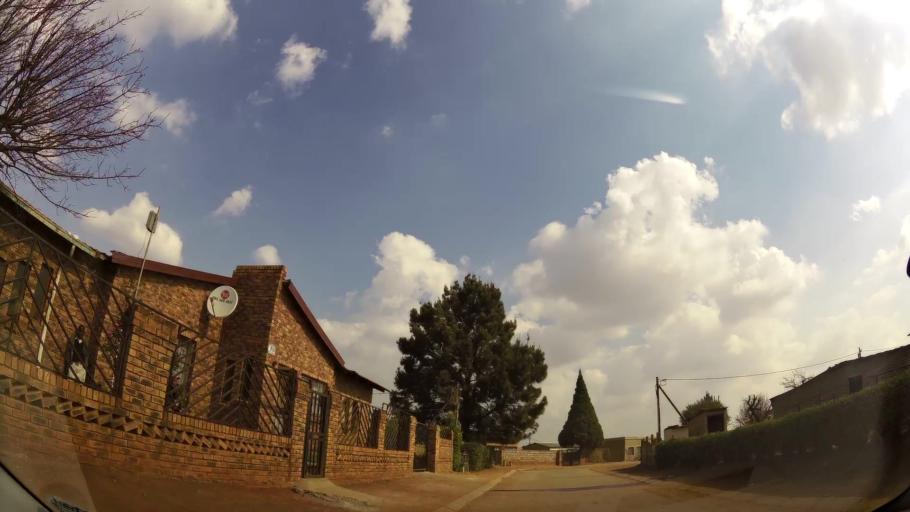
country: ZA
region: Gauteng
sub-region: Ekurhuleni Metropolitan Municipality
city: Springs
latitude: -26.1307
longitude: 28.4756
